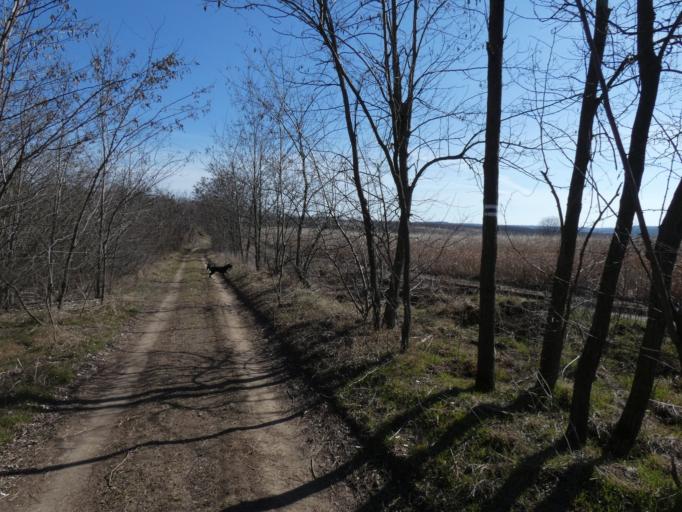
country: HU
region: Pest
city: Pecel
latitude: 47.5097
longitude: 19.3398
